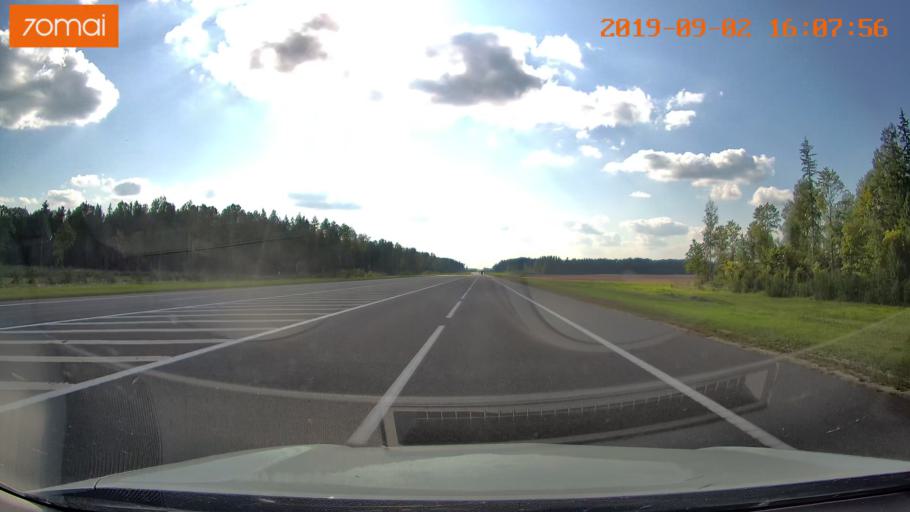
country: BY
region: Minsk
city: Byerazino
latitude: 53.7789
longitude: 28.7430
